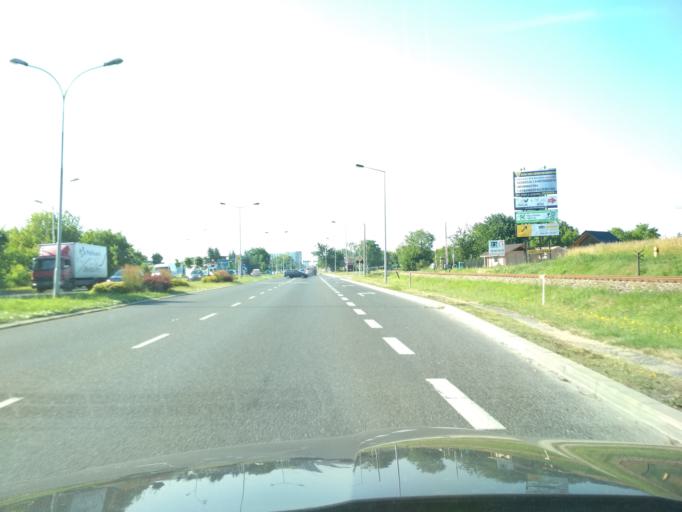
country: PL
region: Subcarpathian Voivodeship
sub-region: Rzeszow
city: Rzeszow
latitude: 50.0645
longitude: 21.9920
